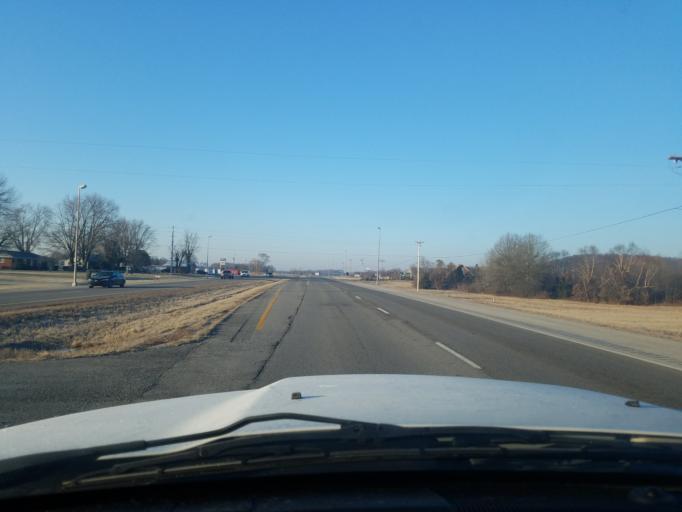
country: US
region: Kentucky
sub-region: Warren County
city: Bowling Green
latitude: 36.9495
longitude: -86.5163
